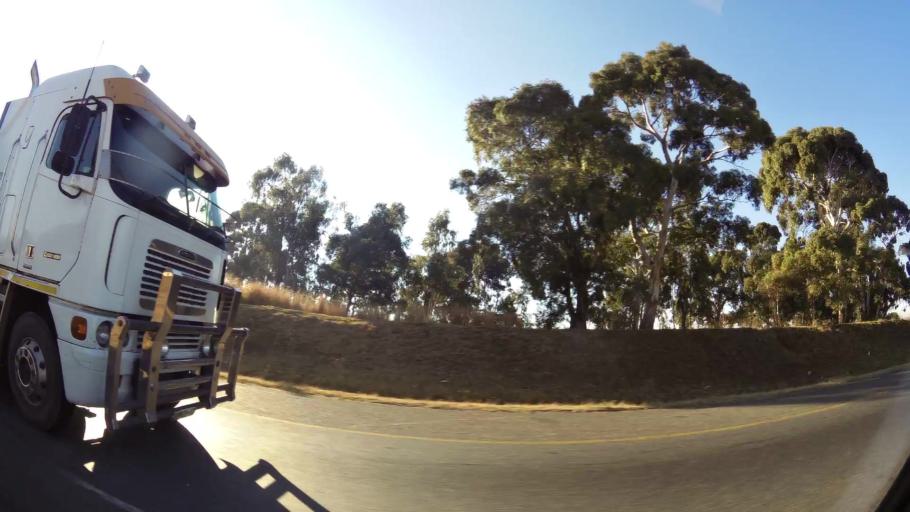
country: ZA
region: Gauteng
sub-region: Ekurhuleni Metropolitan Municipality
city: Germiston
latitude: -26.3250
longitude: 28.1128
